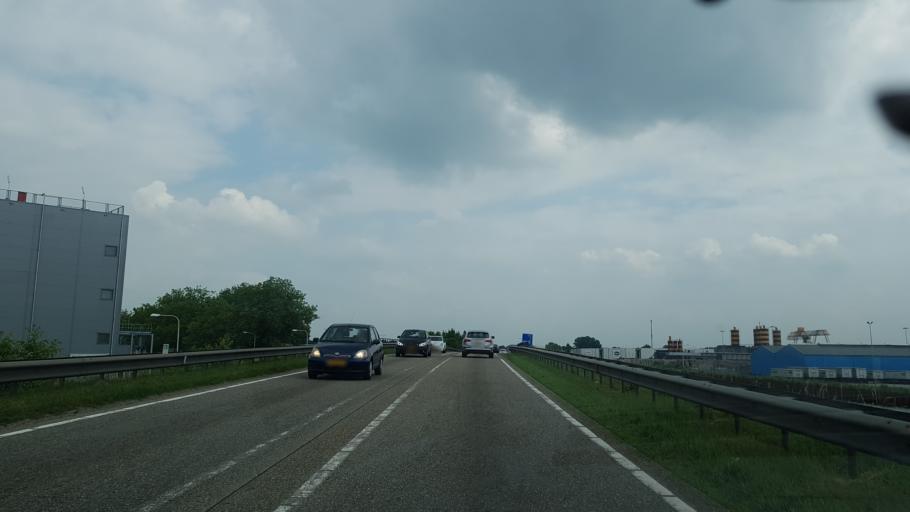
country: NL
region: North Brabant
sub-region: Gemeente Veghel
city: Eerde
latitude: 51.6142
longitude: 5.5217
